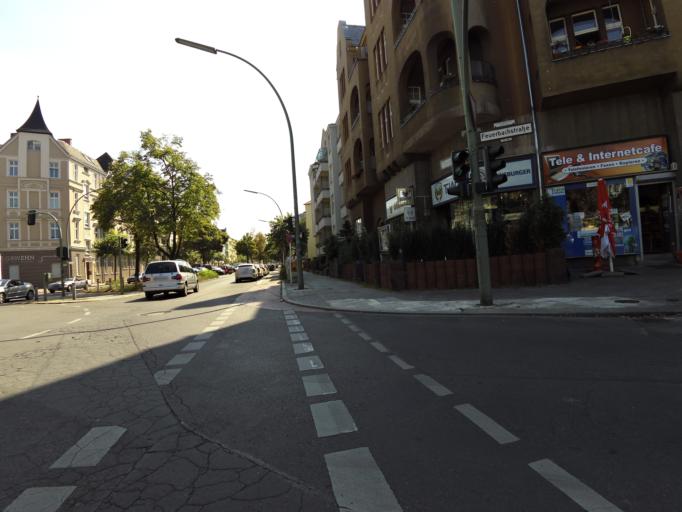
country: DE
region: Berlin
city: Schoneberg Bezirk
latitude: 52.4646
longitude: 13.3399
